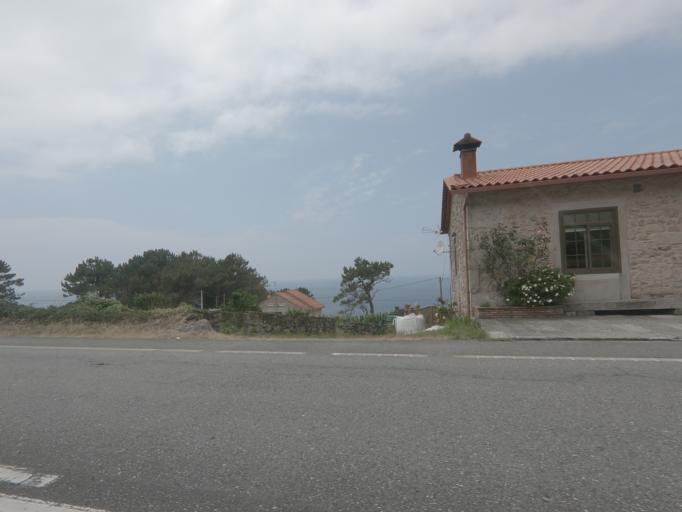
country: ES
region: Galicia
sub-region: Provincia de Pontevedra
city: Oia
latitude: 41.9661
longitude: -8.8836
